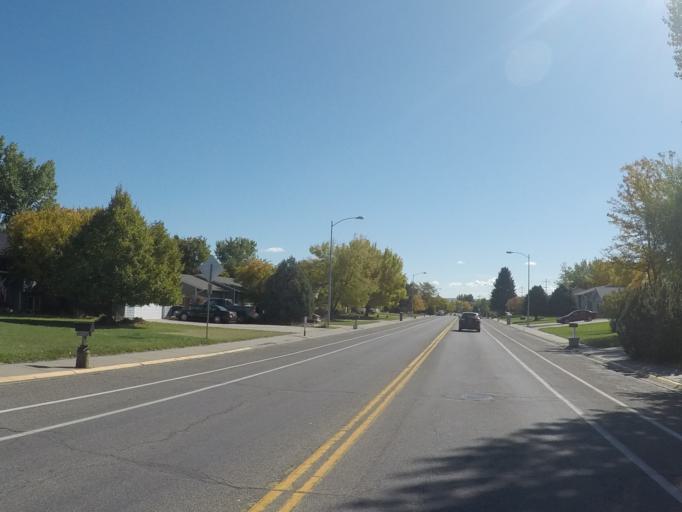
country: US
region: Montana
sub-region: Yellowstone County
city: Billings
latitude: 45.8201
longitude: -108.5054
